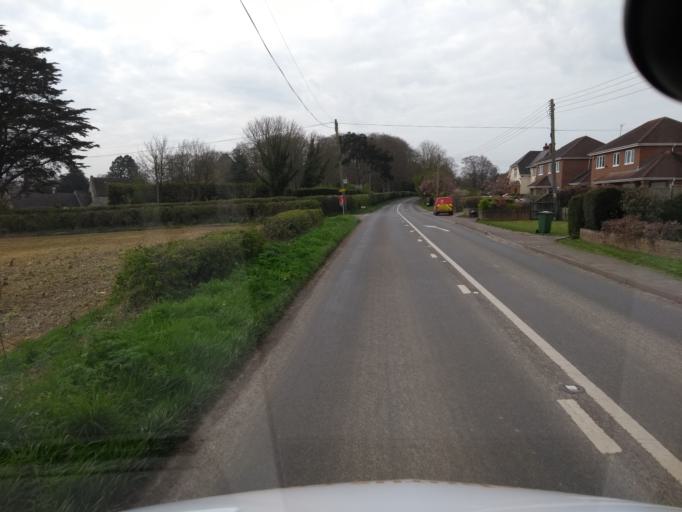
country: GB
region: England
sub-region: Somerset
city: Curry Rivel
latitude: 51.0299
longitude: -2.8518
